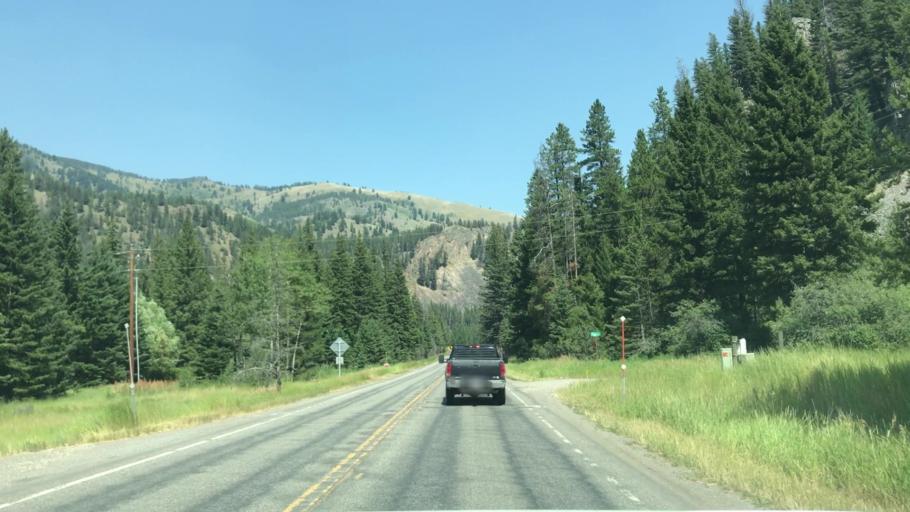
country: US
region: Montana
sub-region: Gallatin County
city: Big Sky
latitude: 45.2907
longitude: -111.2172
